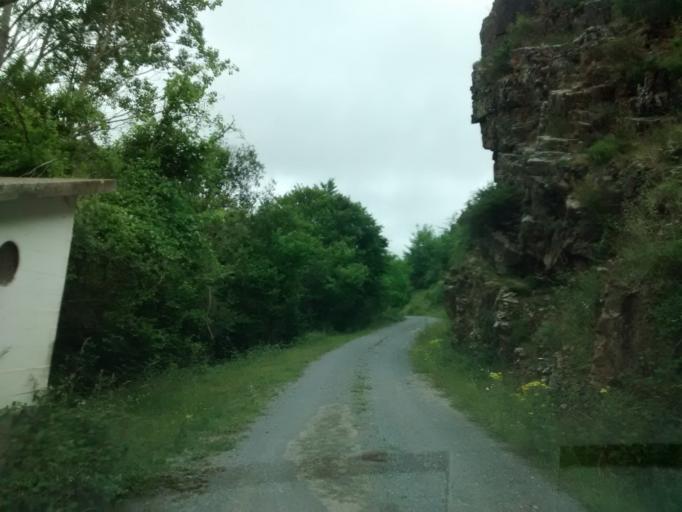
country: ES
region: La Rioja
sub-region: Provincia de La Rioja
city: Ajamil
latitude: 42.1598
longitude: -2.4840
